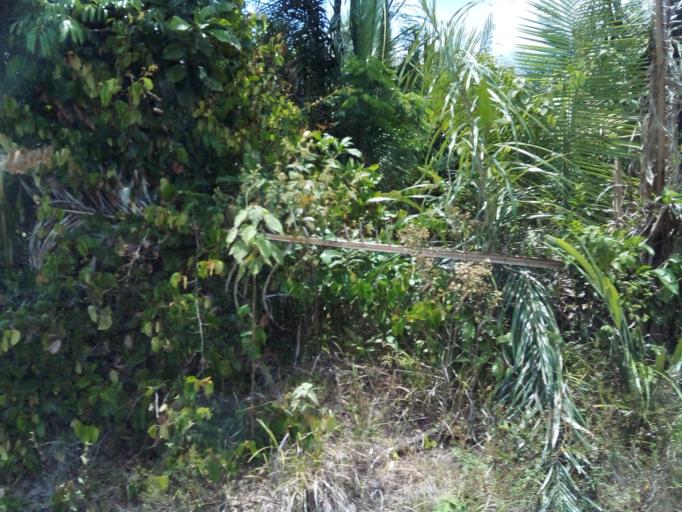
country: BR
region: Maranhao
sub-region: Itapecuru Mirim
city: Itapecuru Mirim
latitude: -3.1355
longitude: -44.3371
